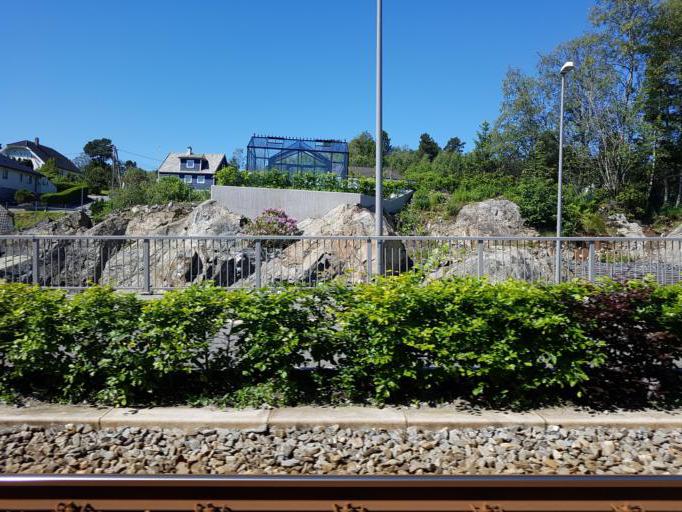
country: NO
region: Hordaland
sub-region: Bergen
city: Ytrebygda
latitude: 60.2921
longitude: 5.2664
